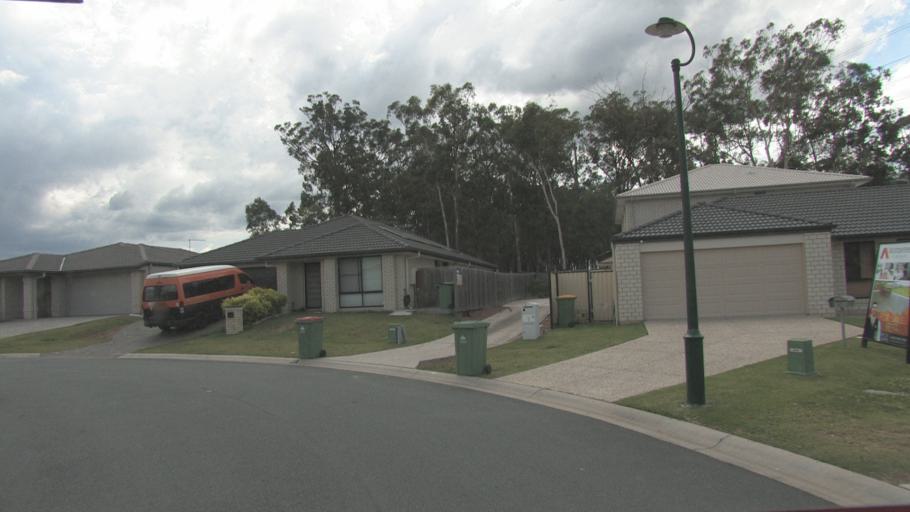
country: AU
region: Queensland
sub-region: Logan
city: Woodridge
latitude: -27.6612
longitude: 153.0861
